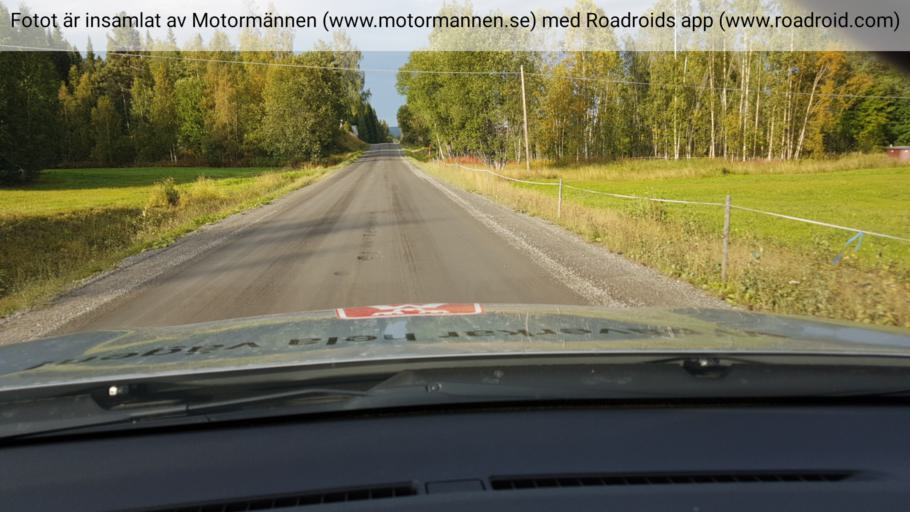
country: SE
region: Jaemtland
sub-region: Stroemsunds Kommun
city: Stroemsund
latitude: 64.0385
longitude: 15.8098
